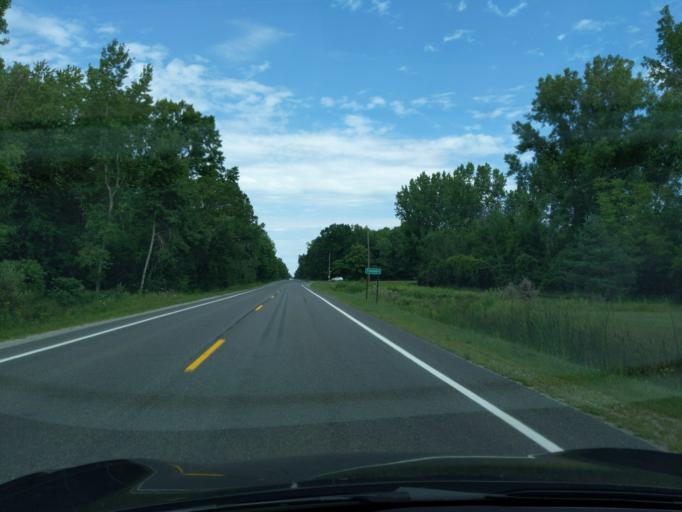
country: US
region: Michigan
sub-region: Midland County
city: Midland
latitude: 43.5236
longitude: -84.3699
